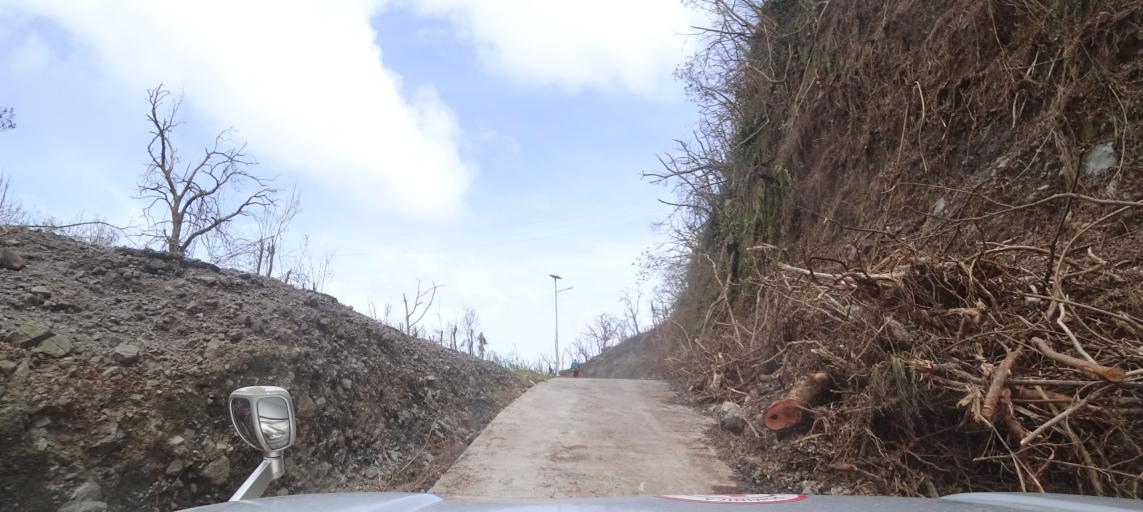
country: DM
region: Saint Patrick
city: La Plaine
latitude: 15.3112
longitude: -61.2502
